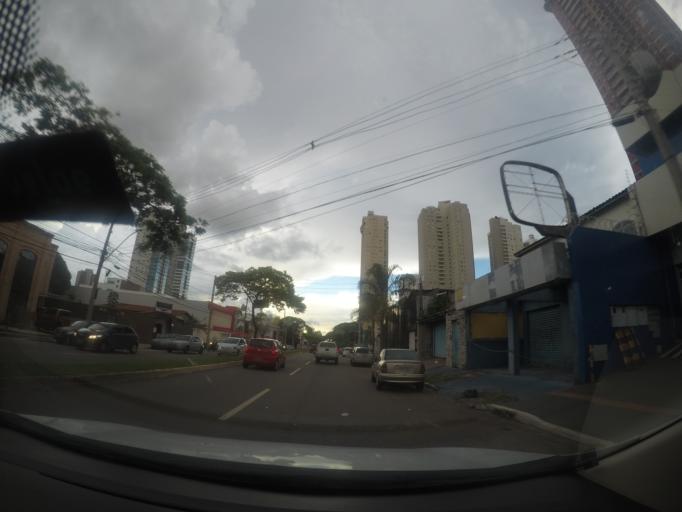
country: BR
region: Goias
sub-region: Goiania
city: Goiania
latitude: -16.7049
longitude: -49.2679
